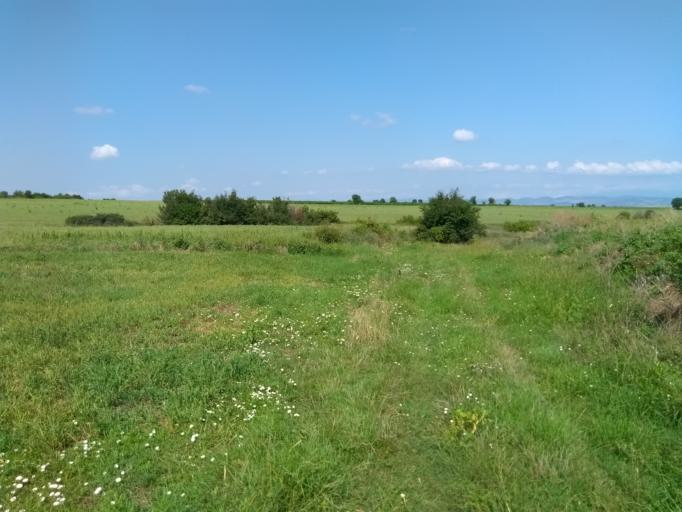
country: BG
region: Sliven
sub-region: Obshtina Sliven
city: Kermen
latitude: 42.4533
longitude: 26.1365
